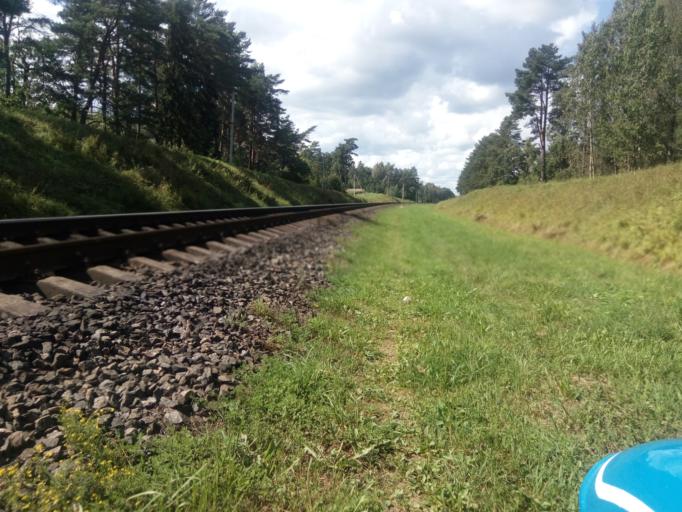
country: BY
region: Vitebsk
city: Dzisna
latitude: 55.6796
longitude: 28.2914
